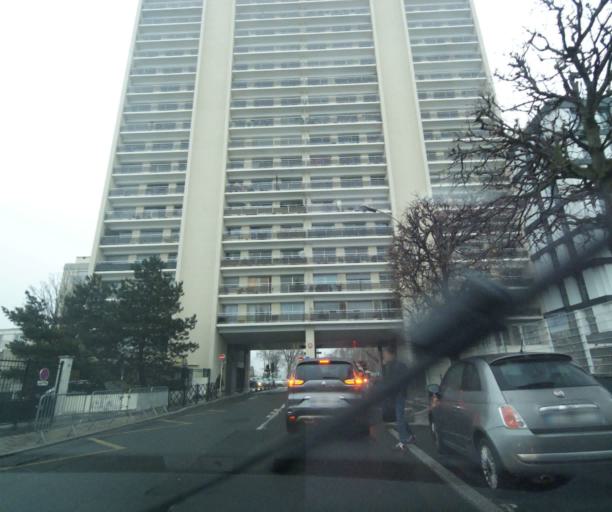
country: FR
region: Ile-de-France
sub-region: Departement des Hauts-de-Seine
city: Bois-Colombes
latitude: 48.9034
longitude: 2.2741
